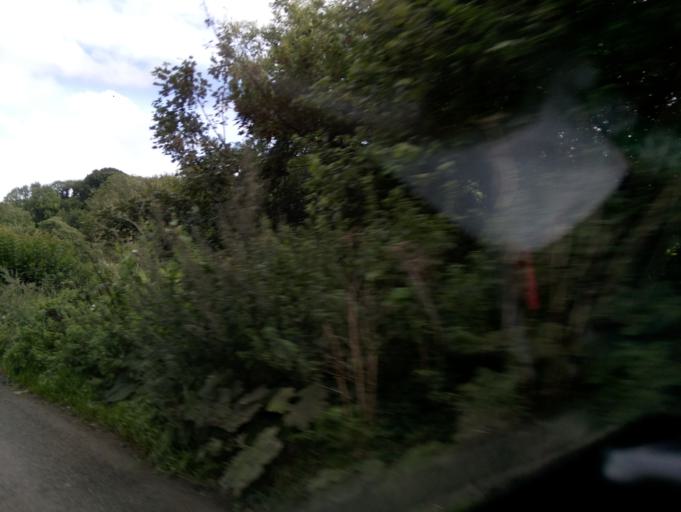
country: GB
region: England
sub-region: Devon
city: Modbury
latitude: 50.3436
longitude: -3.8802
